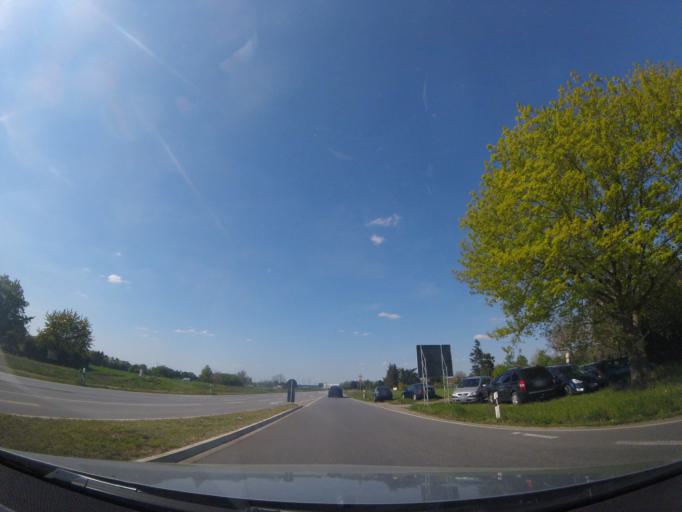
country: DE
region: Hesse
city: Griesheim
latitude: 49.8577
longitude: 8.5475
